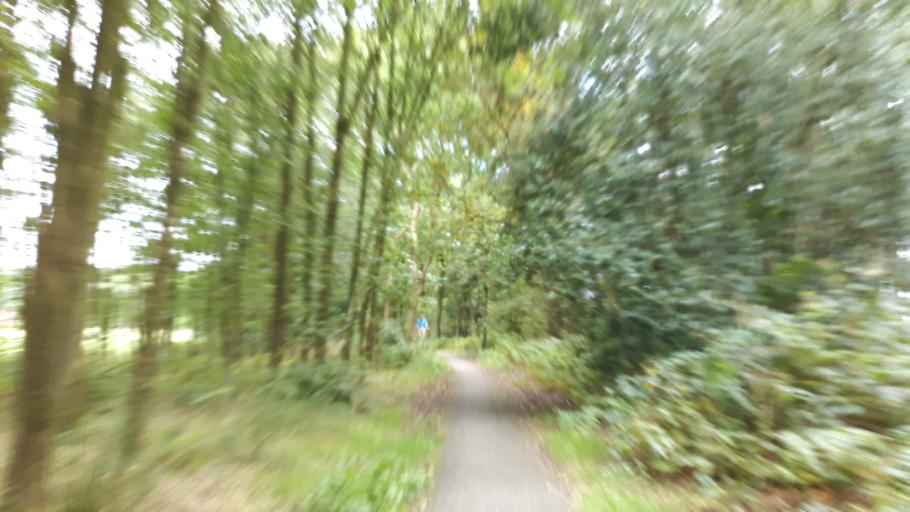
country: NL
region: Friesland
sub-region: Gemeente Smallingerland
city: Drachtstercompagnie
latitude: 53.0613
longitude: 6.2262
